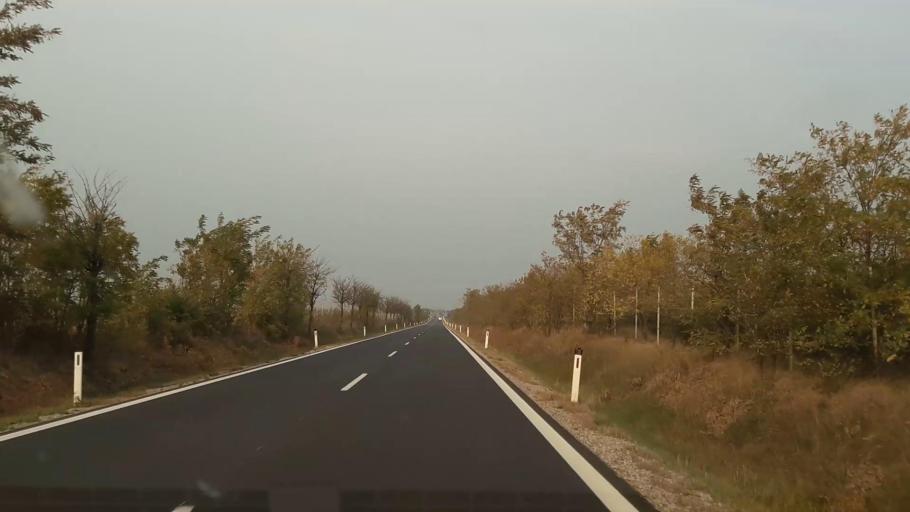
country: AT
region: Burgenland
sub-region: Politischer Bezirk Neusiedl am See
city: Gols
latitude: 47.9380
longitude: 16.9234
